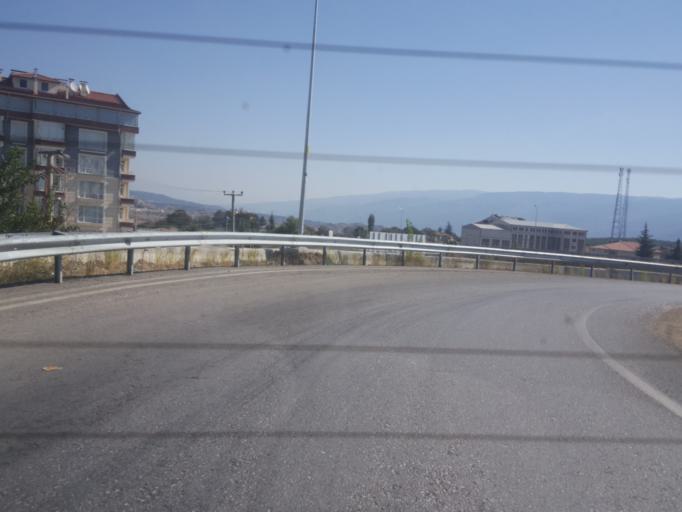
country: TR
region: Kastamonu
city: Tosya
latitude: 41.0079
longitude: 34.0581
